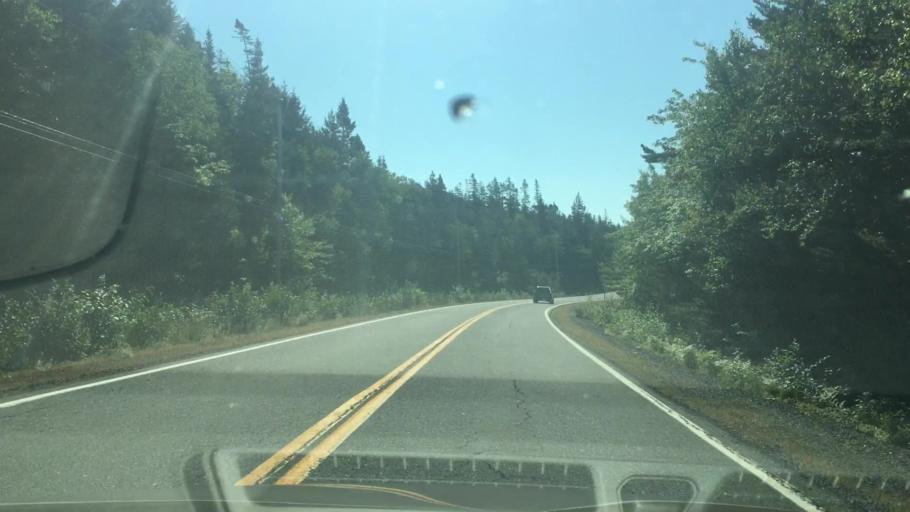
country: CA
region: Nova Scotia
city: Cole Harbour
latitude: 44.8111
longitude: -62.8363
